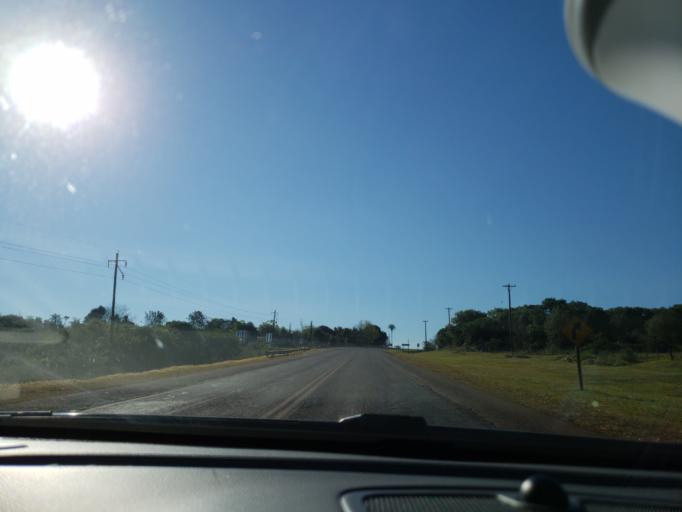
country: AR
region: Misiones
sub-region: Departamento de Apostoles
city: San Jose
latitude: -27.7767
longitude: -55.7733
